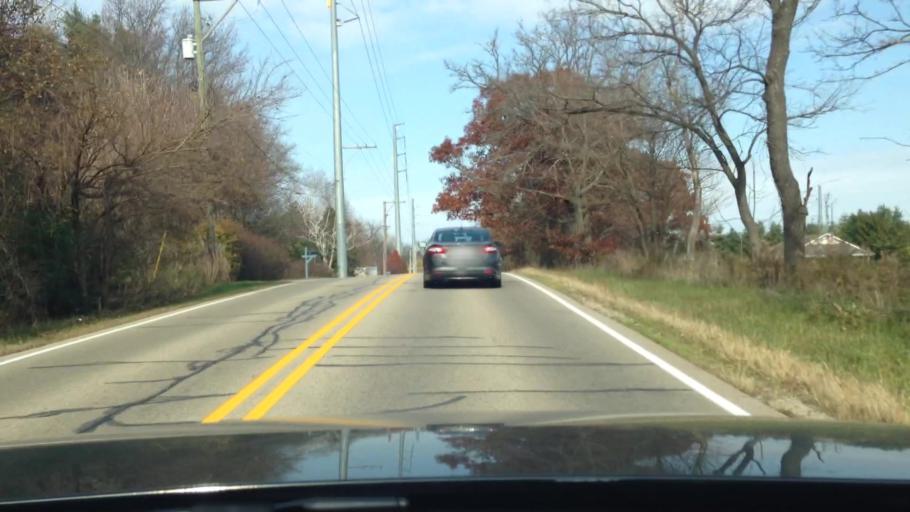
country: US
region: Illinois
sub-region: McHenry County
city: Woodstock
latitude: 42.2951
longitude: -88.4526
